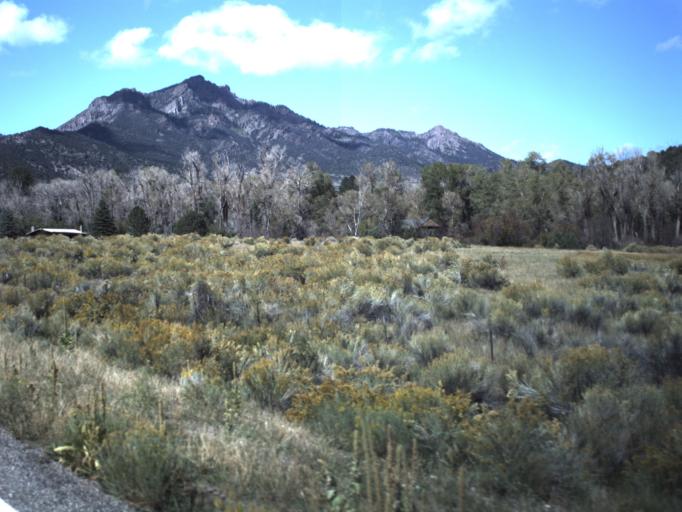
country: US
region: Utah
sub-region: Piute County
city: Junction
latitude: 38.2605
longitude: -112.2929
